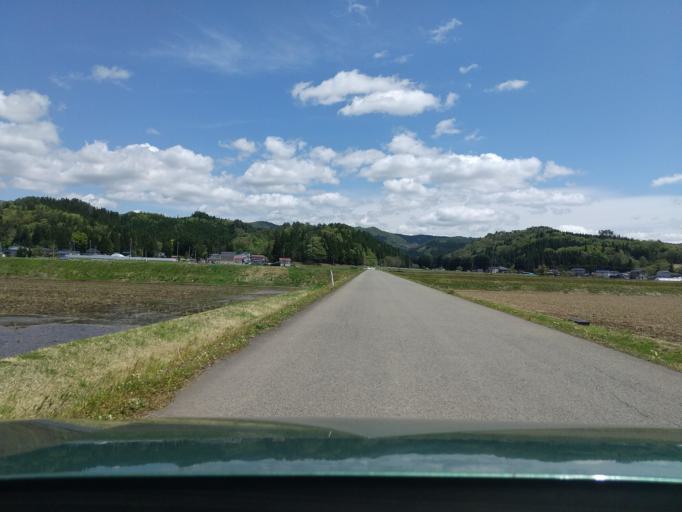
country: JP
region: Akita
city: Yokotemachi
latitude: 39.3434
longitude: 140.5723
